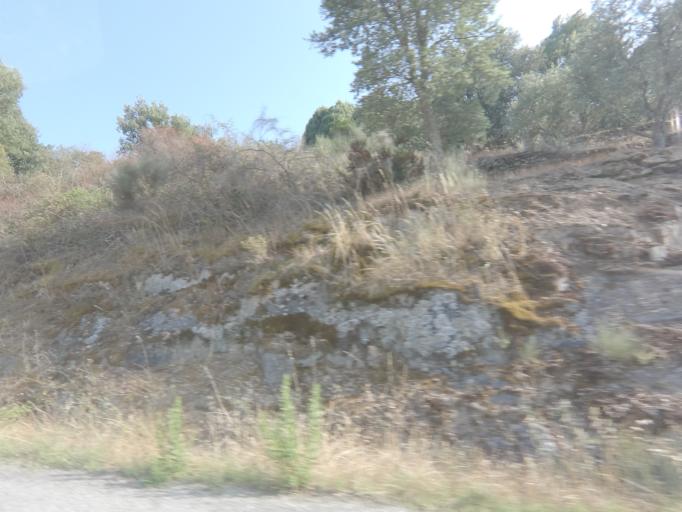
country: PT
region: Viseu
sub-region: Tabuaco
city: Tabuaco
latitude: 41.1319
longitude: -7.5407
